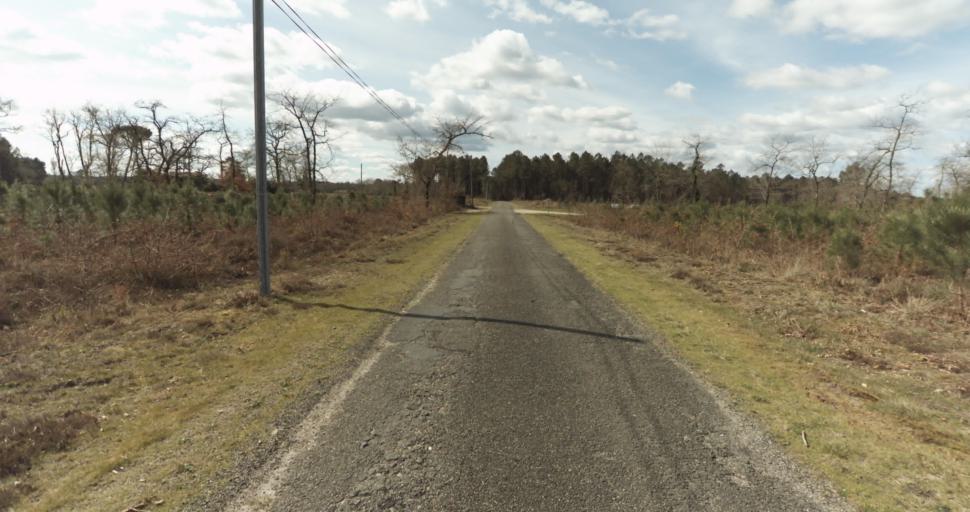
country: FR
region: Aquitaine
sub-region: Departement des Landes
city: Roquefort
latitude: 44.0460
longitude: -0.3698
